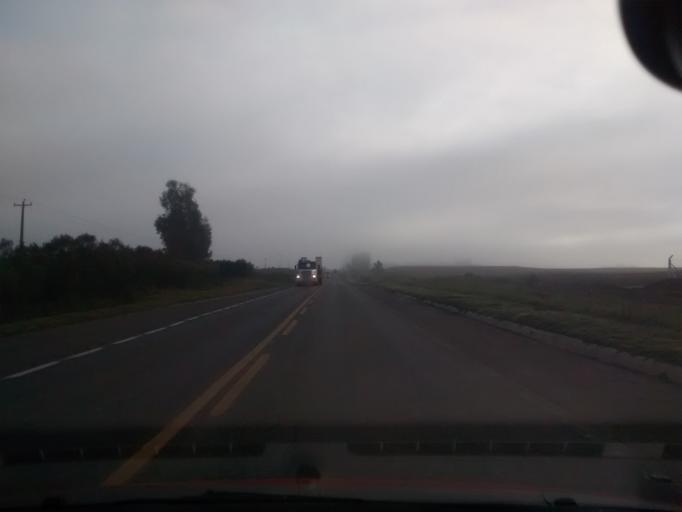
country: BR
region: Rio Grande do Sul
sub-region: Vacaria
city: Vacaria
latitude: -28.4675
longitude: -50.8921
